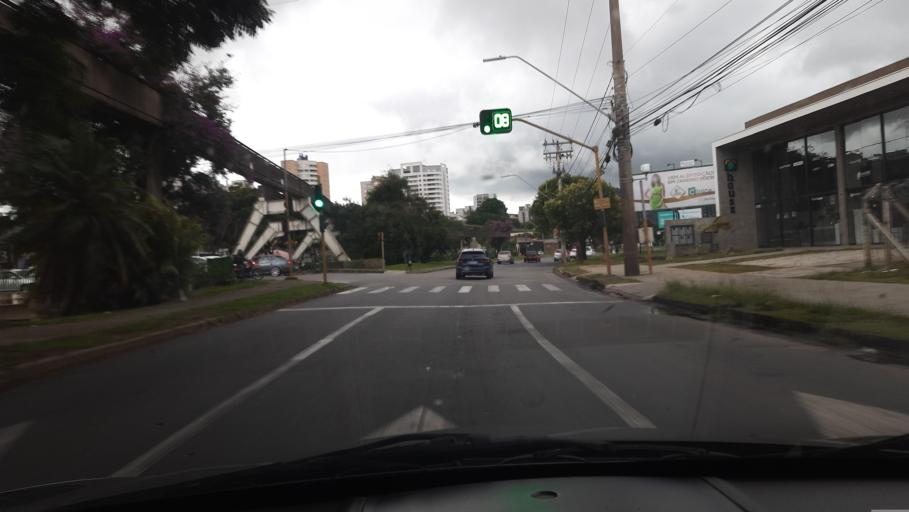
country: BR
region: Minas Gerais
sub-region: Pocos De Caldas
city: Pocos de Caldas
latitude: -21.7844
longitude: -46.5955
